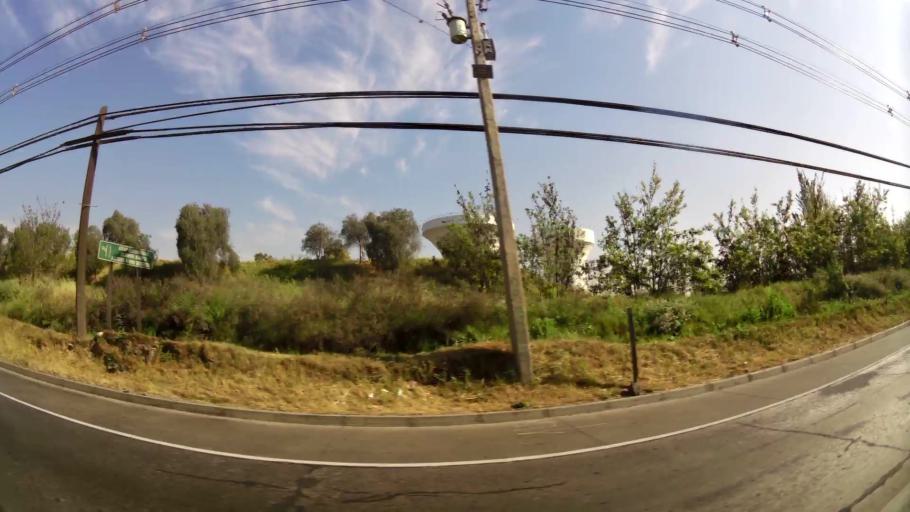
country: CL
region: Santiago Metropolitan
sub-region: Provincia de Maipo
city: San Bernardo
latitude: -33.5308
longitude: -70.7621
